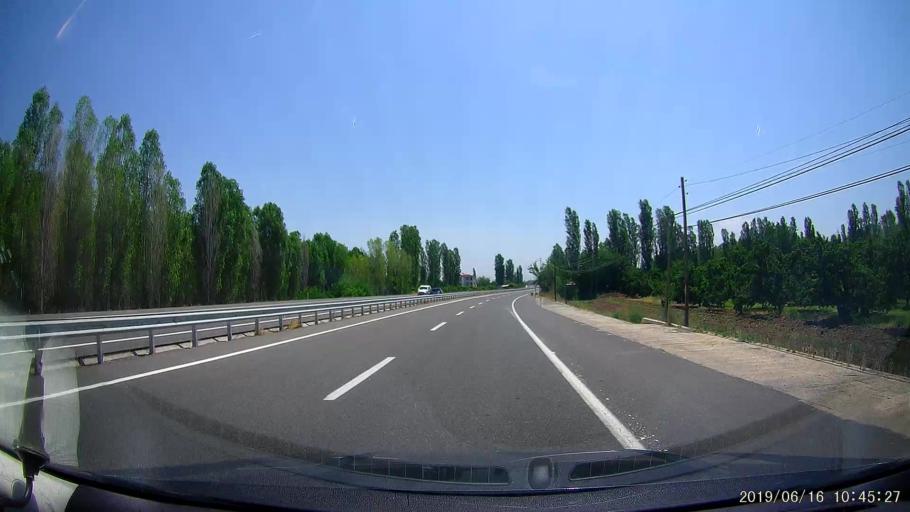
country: AM
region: Armavir
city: Shenavan
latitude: 40.0275
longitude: 43.8692
